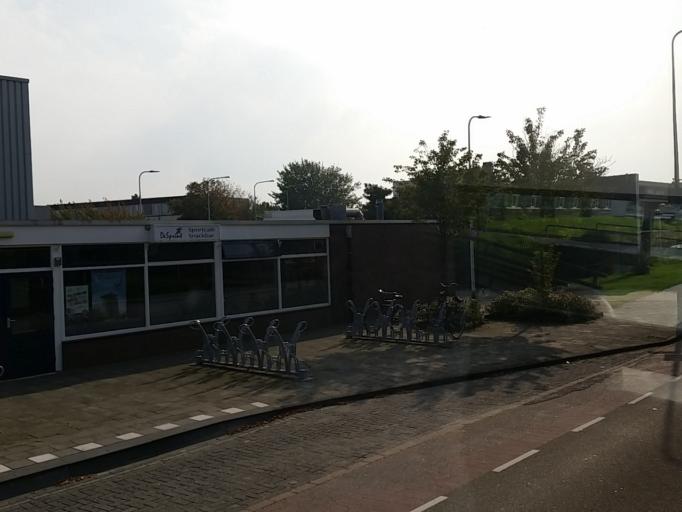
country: NL
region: South Holland
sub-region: Gemeente Noordwijk
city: Noordwijk-Binnen
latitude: 52.2417
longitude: 4.4473
